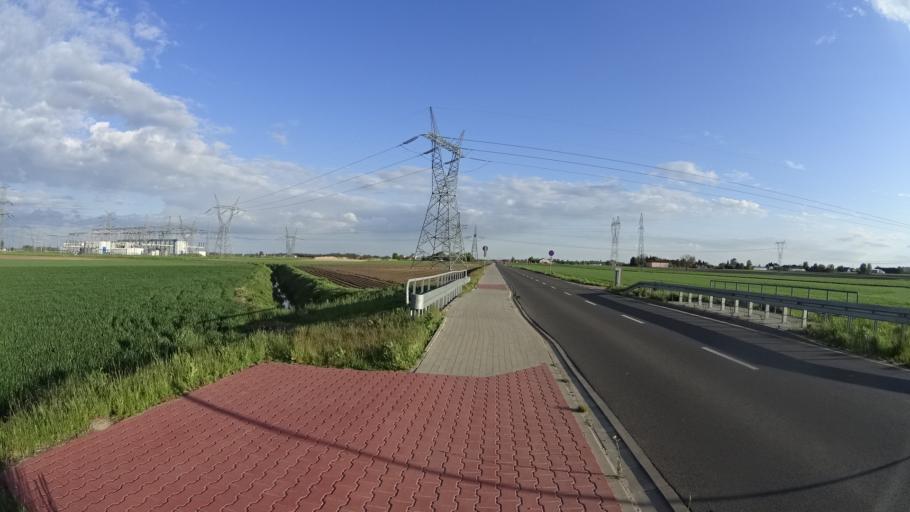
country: PL
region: Masovian Voivodeship
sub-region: Powiat warszawski zachodni
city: Jozefow
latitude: 52.2295
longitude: 20.7377
